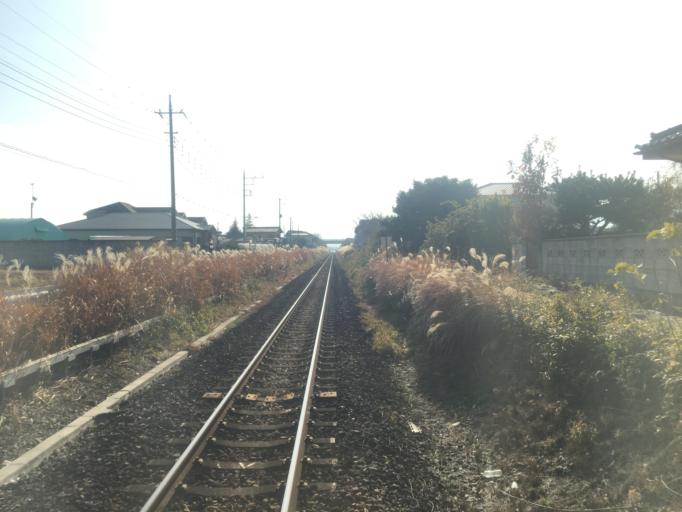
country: JP
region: Gunma
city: Fujioka
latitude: 36.2363
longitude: 139.0830
